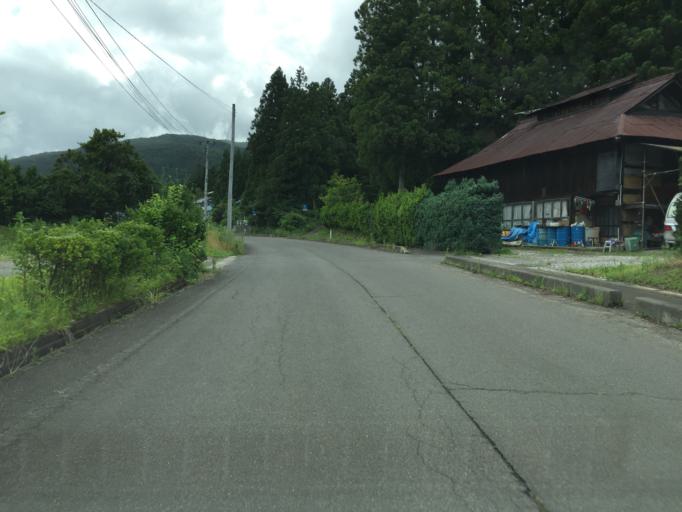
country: JP
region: Fukushima
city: Fukushima-shi
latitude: 37.7329
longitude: 140.3663
